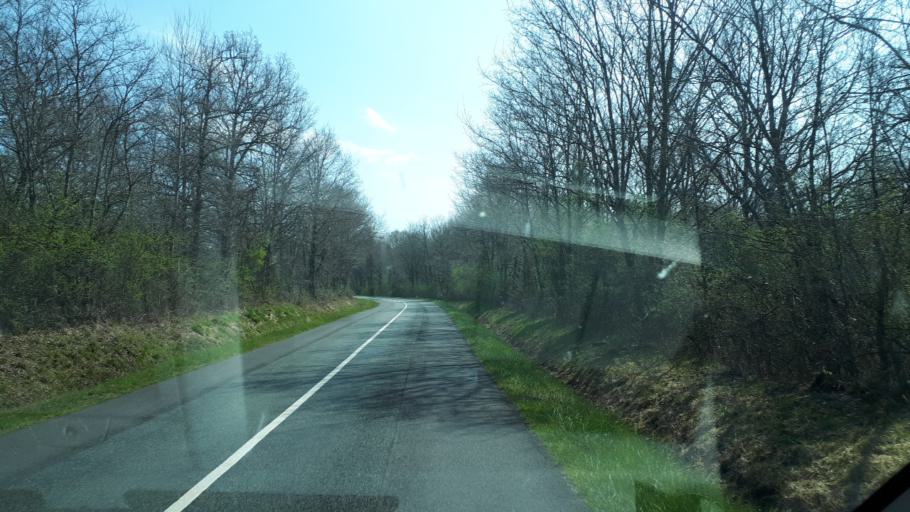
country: FR
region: Centre
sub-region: Departement du Loir-et-Cher
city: Selles-Saint-Denis
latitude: 47.3517
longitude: 1.8624
